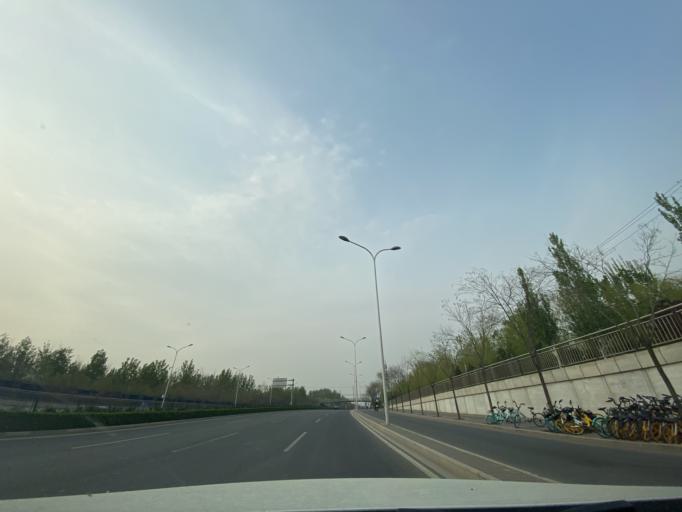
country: CN
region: Beijing
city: Babaoshan
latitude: 39.9330
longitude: 116.2209
